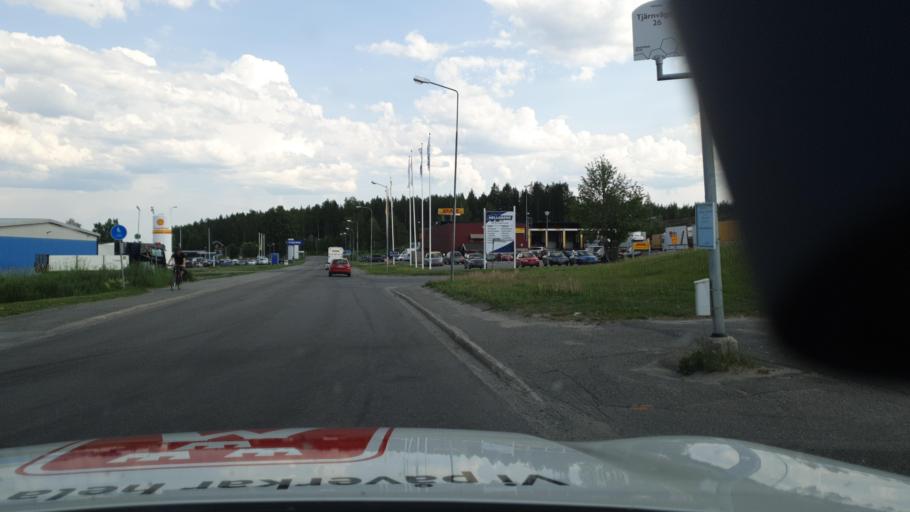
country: SE
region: Vaesterbotten
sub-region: Skelleftea Kommun
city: Skelleftea
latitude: 64.7321
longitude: 20.9675
